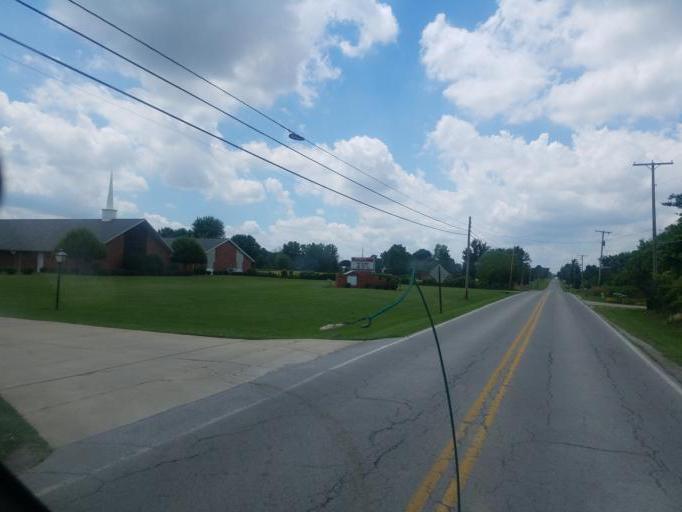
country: US
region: Ohio
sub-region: Huron County
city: Willard
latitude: 41.0546
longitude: -82.7502
